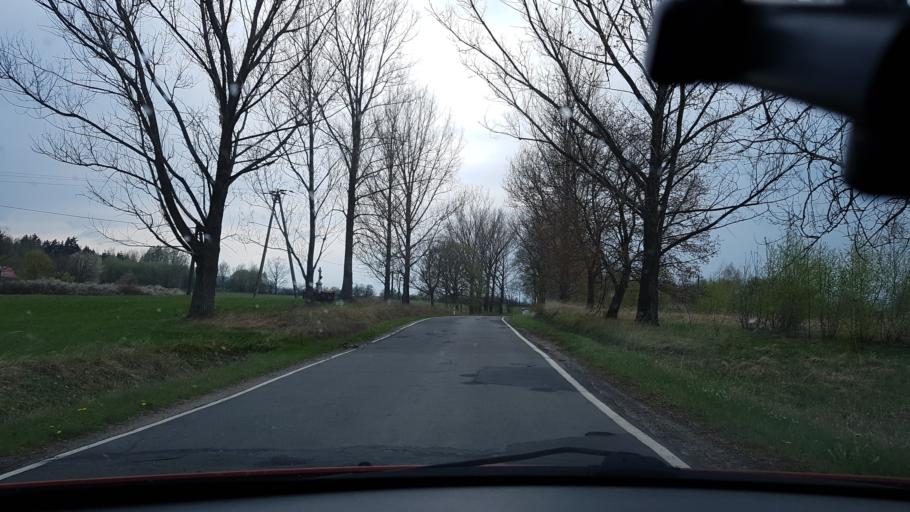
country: PL
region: Lower Silesian Voivodeship
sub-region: Powiat klodzki
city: Bystrzyca Klodzka
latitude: 50.3229
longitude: 16.6103
